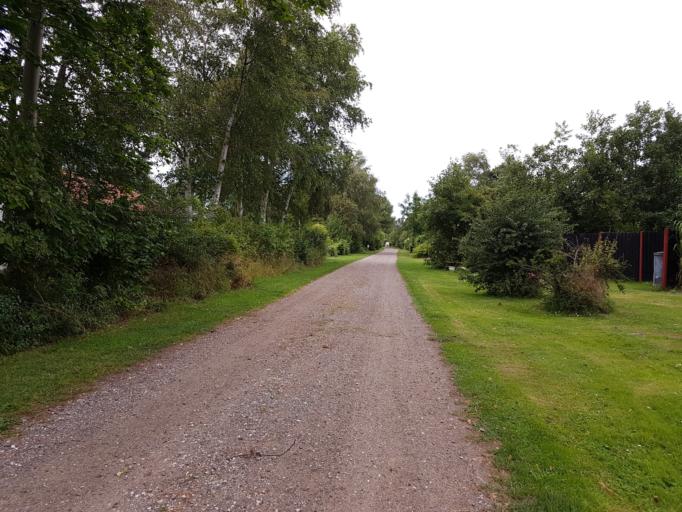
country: DK
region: Zealand
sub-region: Guldborgsund Kommune
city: Nykobing Falster
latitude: 54.5906
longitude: 11.9616
